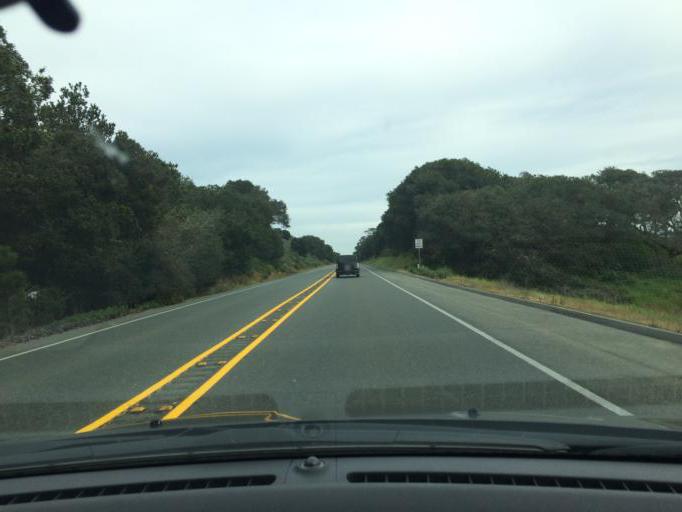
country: US
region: California
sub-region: Monterey County
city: Prunedale
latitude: 36.7777
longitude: -121.7112
